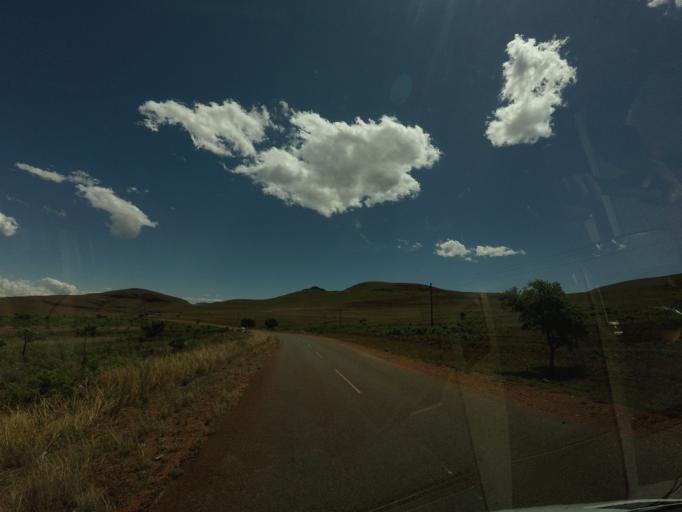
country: ZA
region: Limpopo
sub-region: Mopani District Municipality
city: Hoedspruit
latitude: -24.6242
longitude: 30.8126
